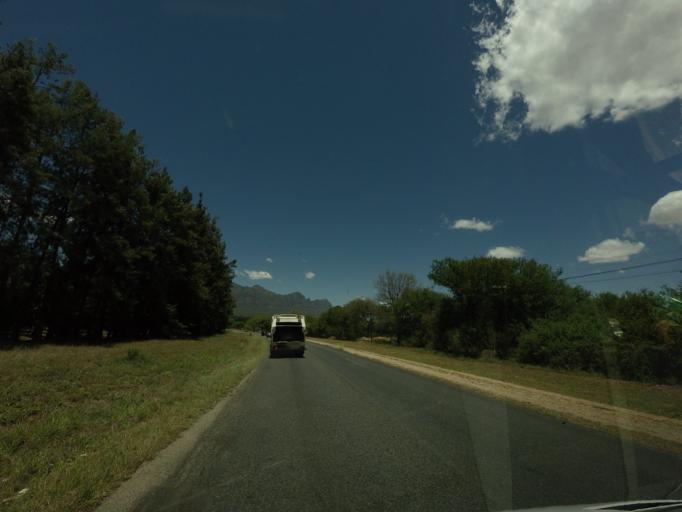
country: ZA
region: Limpopo
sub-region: Mopani District Municipality
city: Hoedspruit
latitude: -24.3993
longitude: 30.8063
